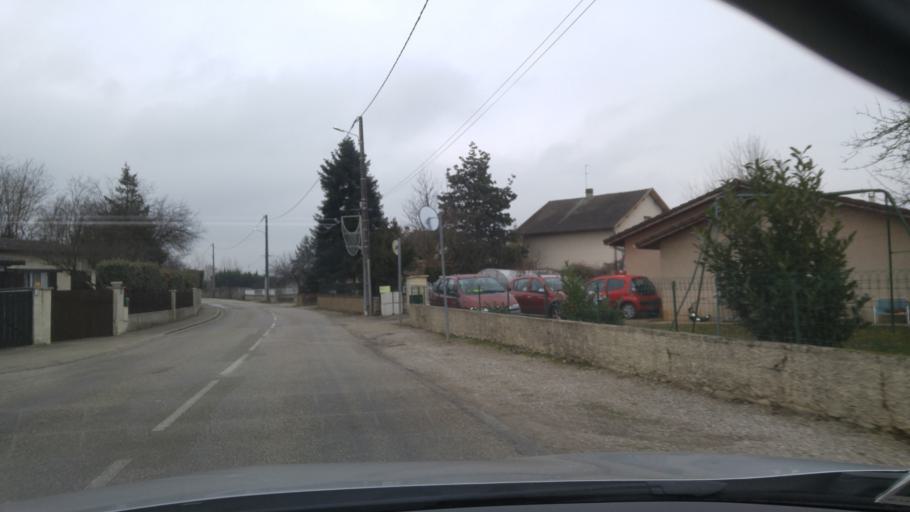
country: FR
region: Rhone-Alpes
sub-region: Departement de l'Isere
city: Charvieu-Chavagneux
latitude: 45.7288
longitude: 5.1419
